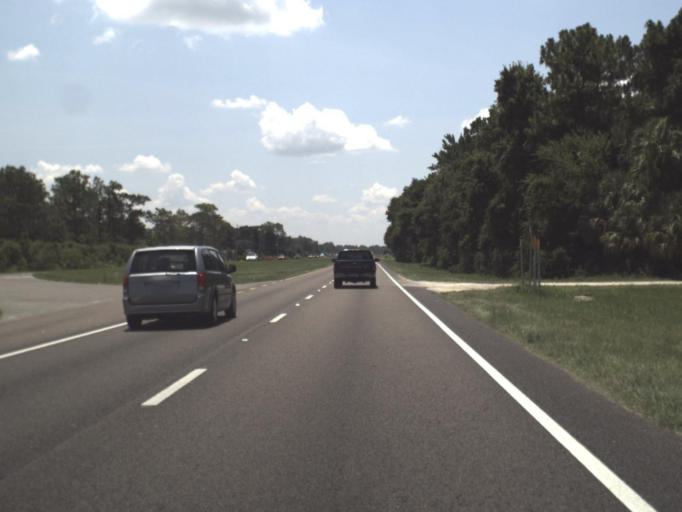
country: US
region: Florida
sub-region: Citrus County
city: Homosassa Springs
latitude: 28.7894
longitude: -82.5669
